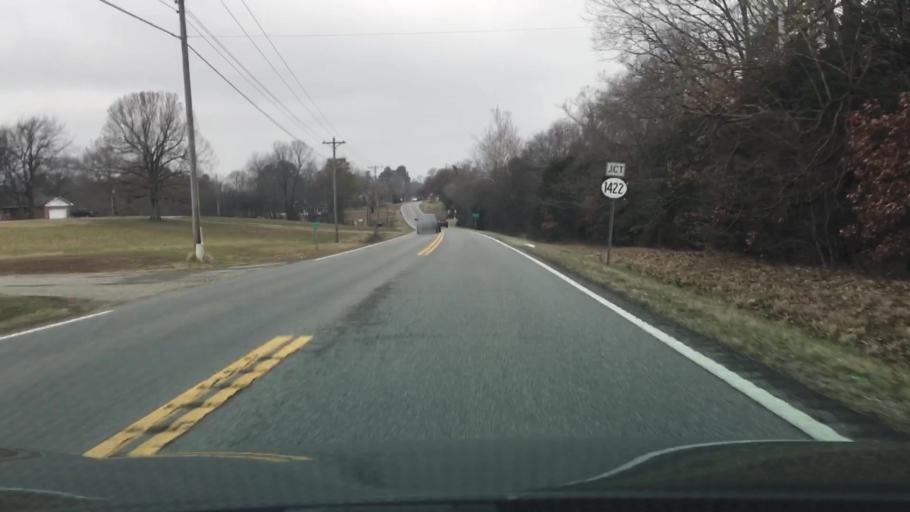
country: US
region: Kentucky
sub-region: Marshall County
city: Calvert City
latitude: 36.9560
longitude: -88.3723
